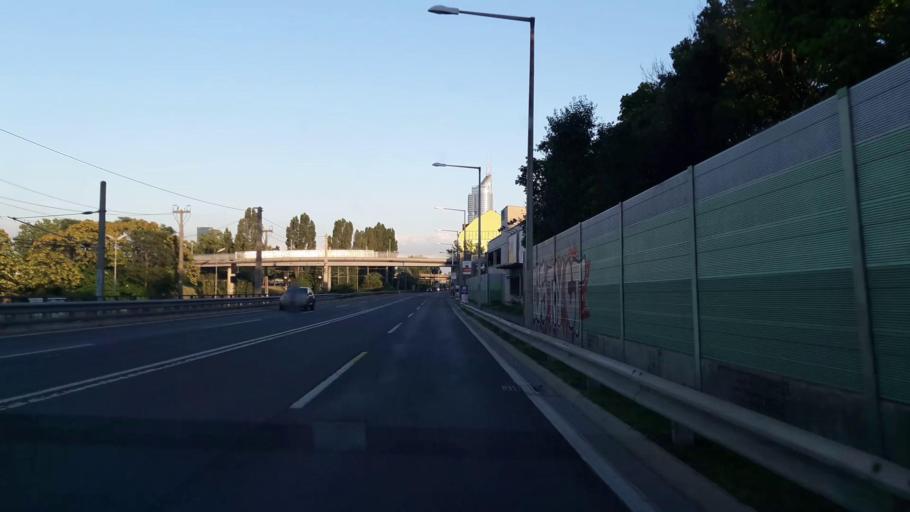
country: AT
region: Vienna
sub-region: Wien Stadt
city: Vienna
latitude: 48.2490
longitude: 16.3785
